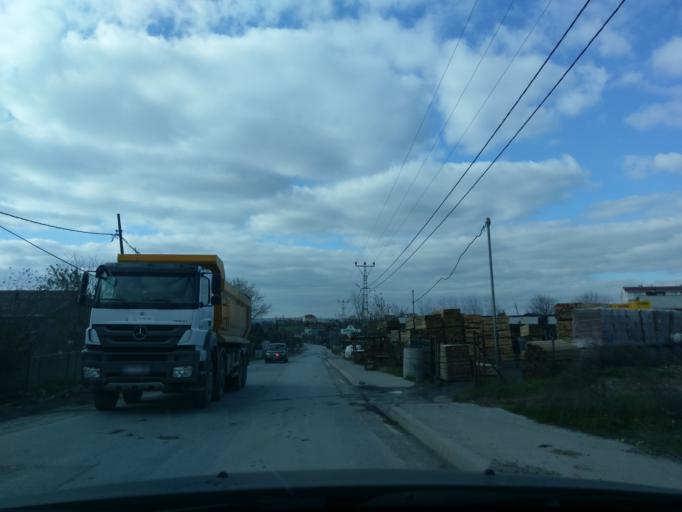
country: TR
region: Istanbul
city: Durusu
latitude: 41.2644
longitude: 28.6854
